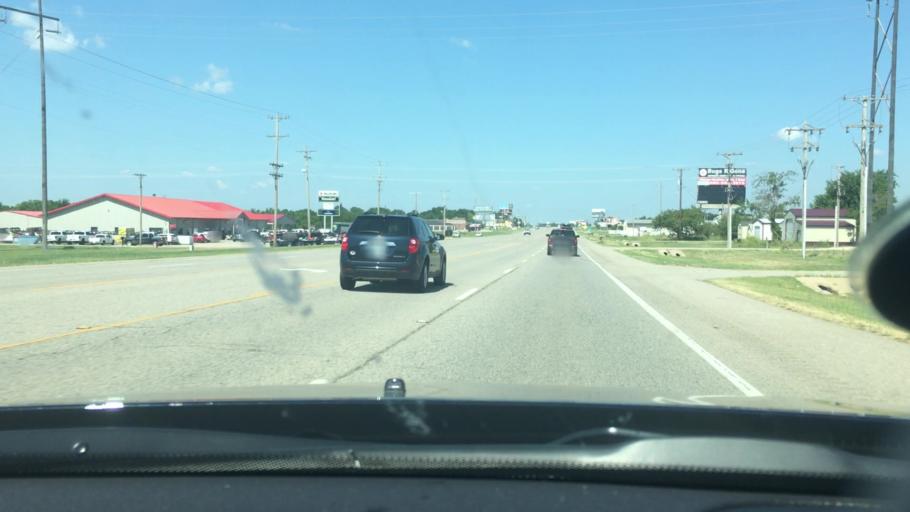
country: US
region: Oklahoma
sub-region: Bryan County
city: Calera
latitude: 33.9980
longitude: -96.4556
